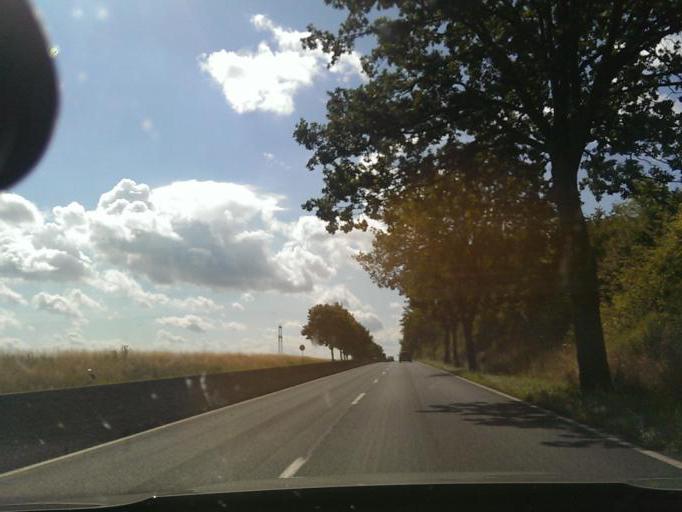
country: DE
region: Lower Saxony
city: Laatzen
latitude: 52.2859
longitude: 9.8379
